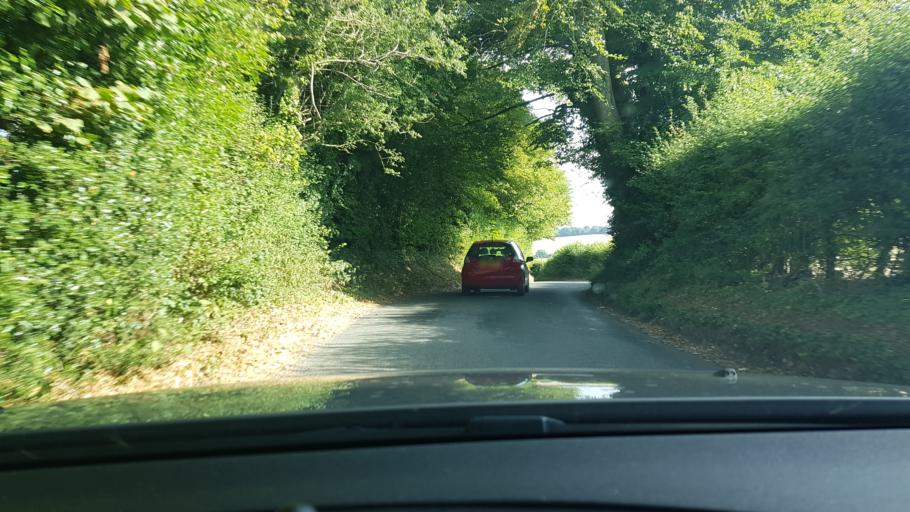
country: GB
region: England
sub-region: Wiltshire
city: Ramsbury
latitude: 51.4512
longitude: -1.5934
